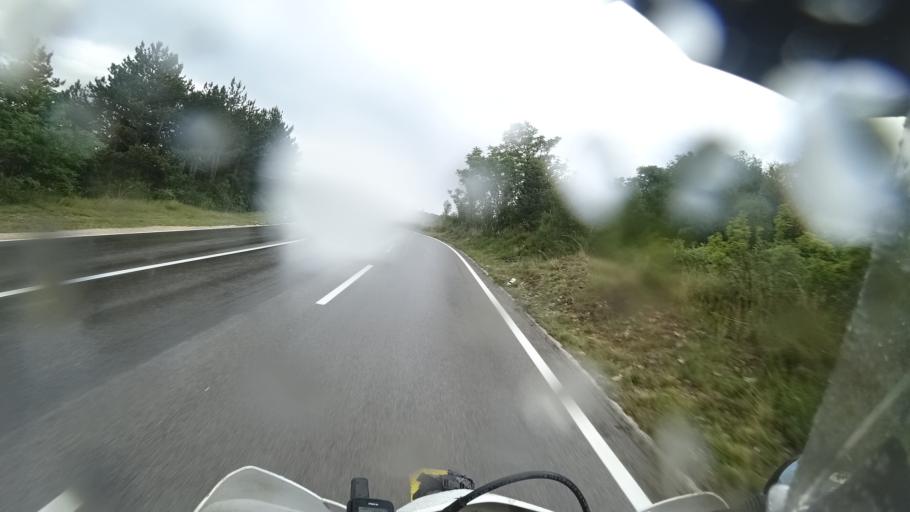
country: HR
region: Sibensko-Kniniska
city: Knin
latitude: 44.0414
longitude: 16.1848
